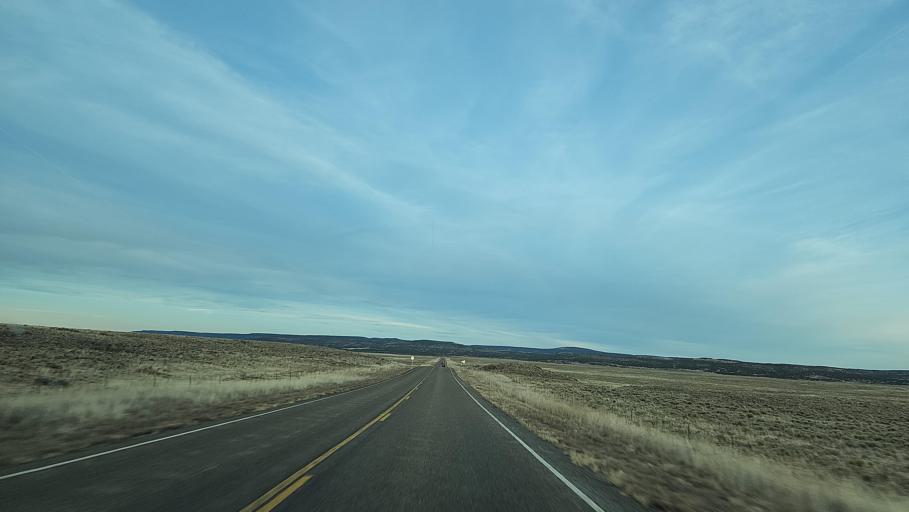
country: US
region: New Mexico
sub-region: Cibola County
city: Grants
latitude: 34.6993
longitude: -108.0406
